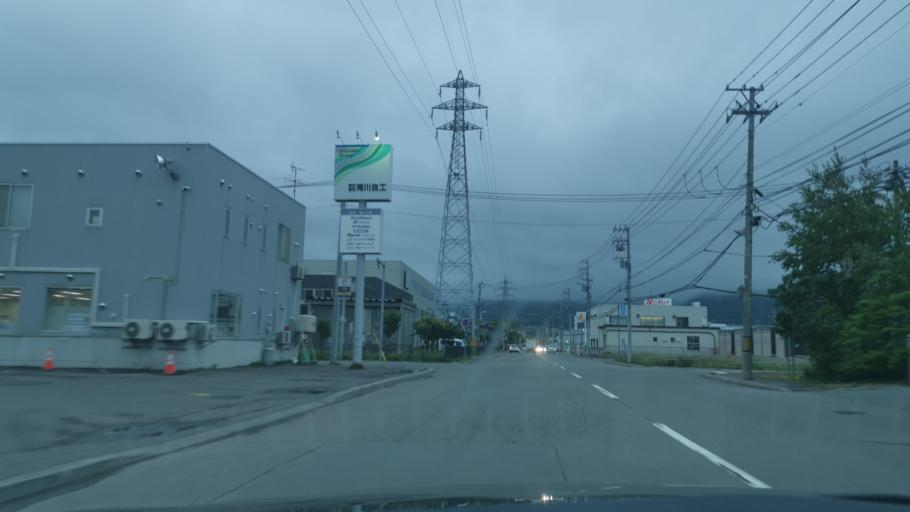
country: JP
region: Hokkaido
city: Sapporo
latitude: 43.1083
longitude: 141.2834
